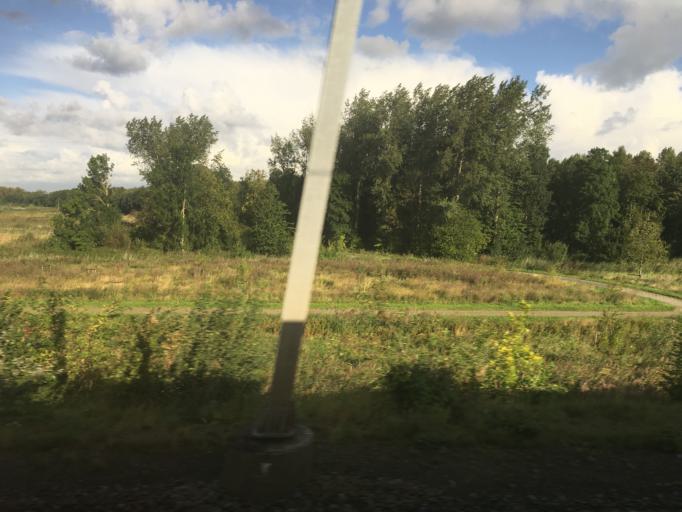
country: NL
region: Flevoland
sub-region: Gemeente Almere
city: Almere Stad
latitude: 52.4090
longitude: 5.3146
